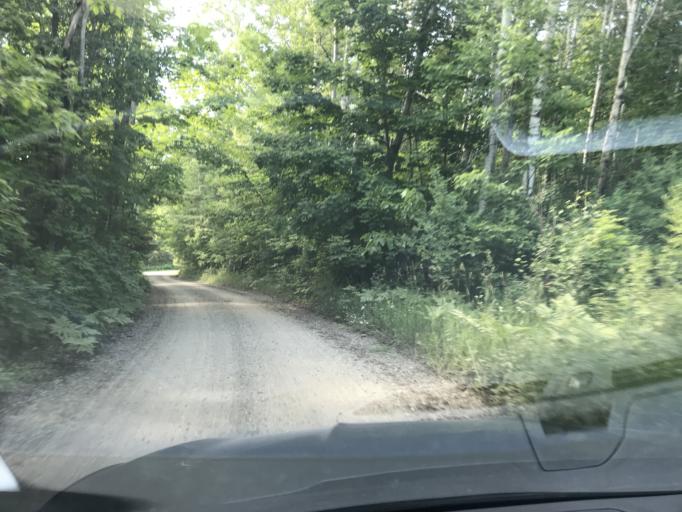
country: US
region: Michigan
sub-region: Cheboygan County
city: Cheboygan
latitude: 45.6227
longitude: -84.6773
